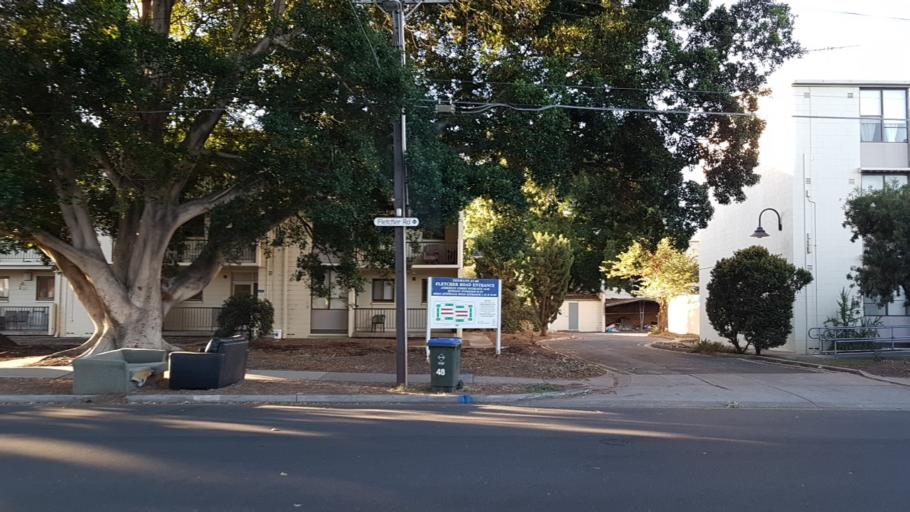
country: AU
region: South Australia
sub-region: Charles Sturt
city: Henley Beach
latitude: -34.9280
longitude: 138.5066
